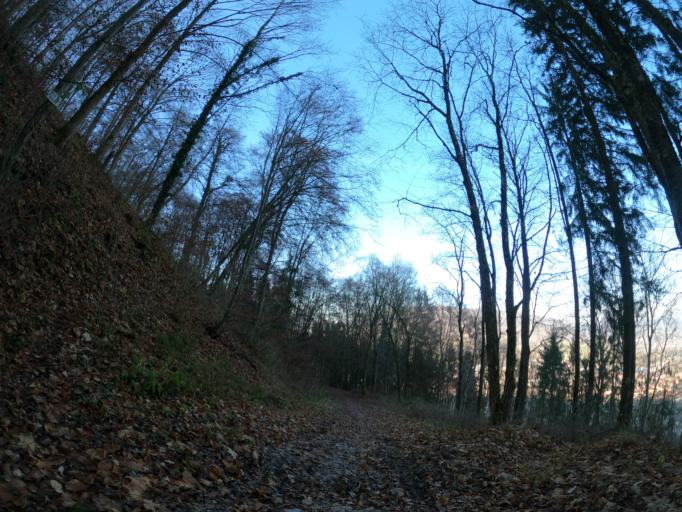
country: DE
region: Baden-Wuerttemberg
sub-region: Regierungsbezirk Stuttgart
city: Deggingen
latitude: 48.5911
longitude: 9.7250
